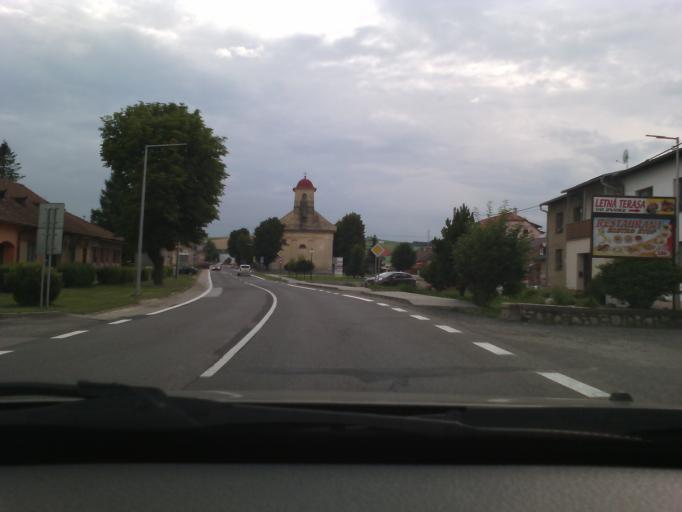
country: SK
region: Presovsky
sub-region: Okres Presov
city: Kezmarok
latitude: 49.1166
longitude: 20.3788
